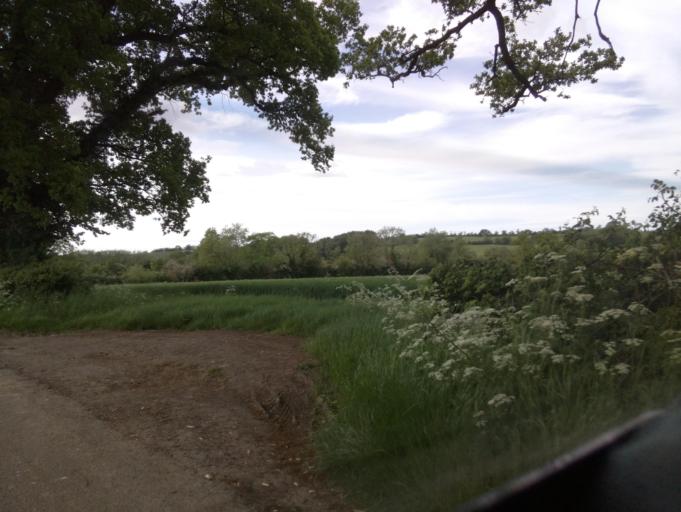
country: GB
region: England
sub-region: Gloucestershire
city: Moreton in Marsh
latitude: 52.0259
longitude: -1.7148
